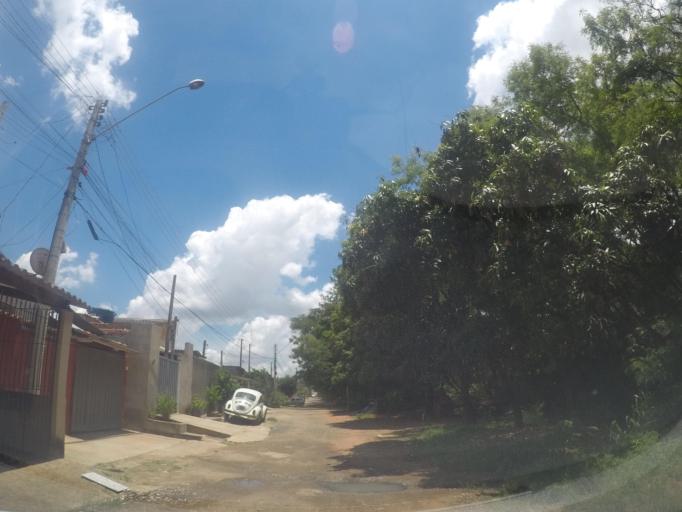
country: BR
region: Sao Paulo
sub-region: Sumare
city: Sumare
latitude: -22.8159
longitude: -47.2340
